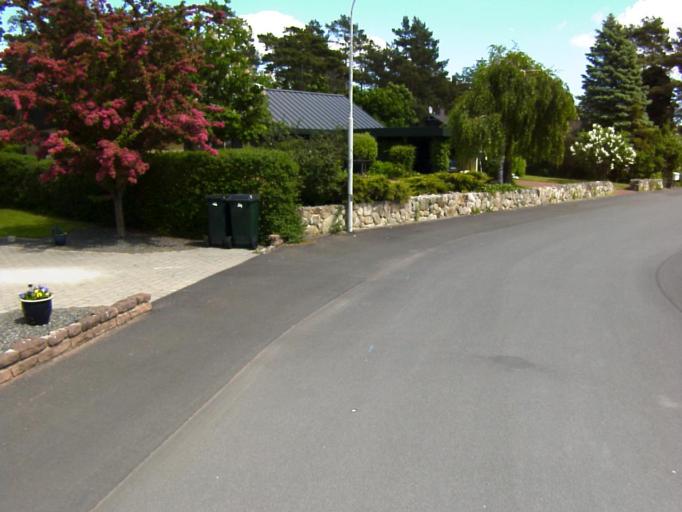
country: SE
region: Skane
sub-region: Kristianstads Kommun
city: Ahus
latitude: 55.9480
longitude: 14.2726
